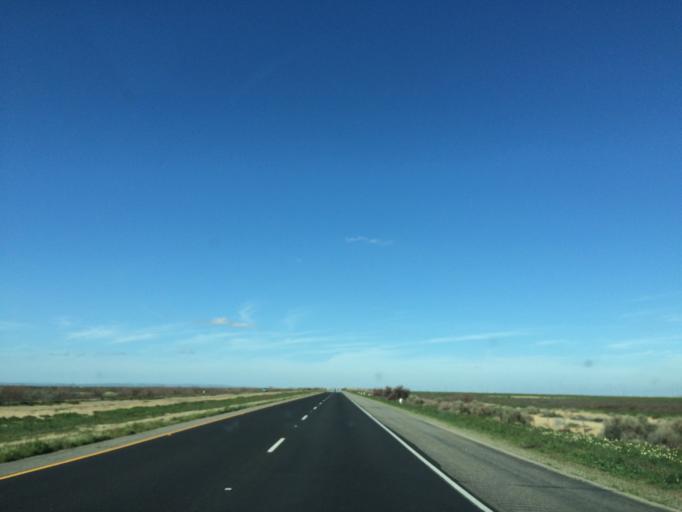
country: US
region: California
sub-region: Kern County
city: Lost Hills
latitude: 35.7754
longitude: -119.7715
